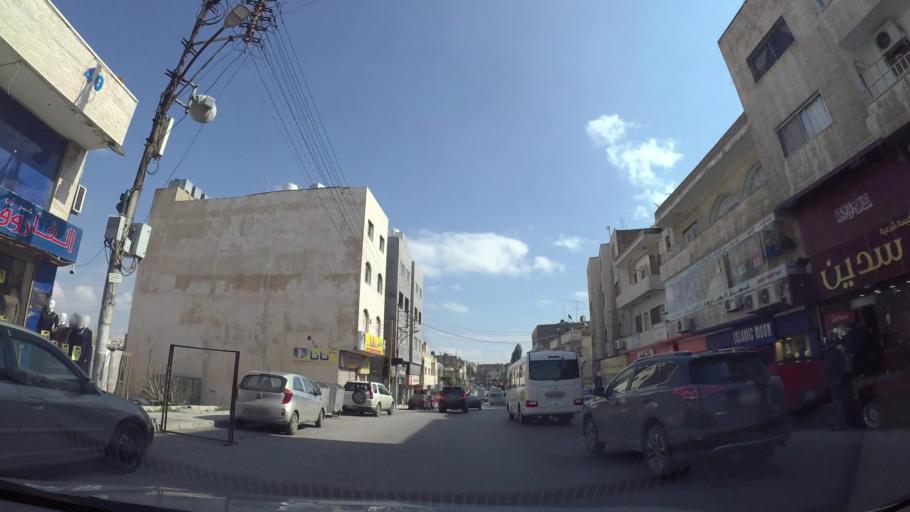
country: JO
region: Amman
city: Al Jubayhah
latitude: 32.0231
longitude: 35.8401
